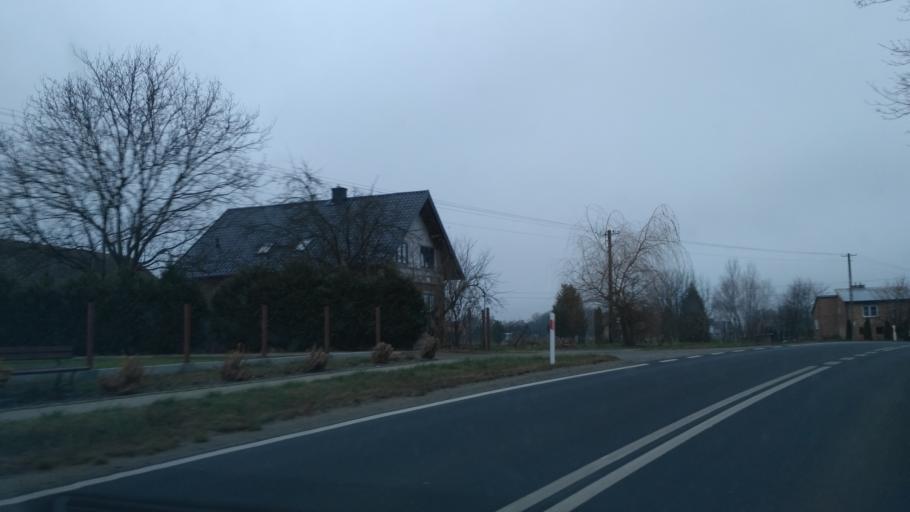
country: PL
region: Subcarpathian Voivodeship
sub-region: Powiat jaroslawski
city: Pruchnik
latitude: 49.9206
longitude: 22.5667
